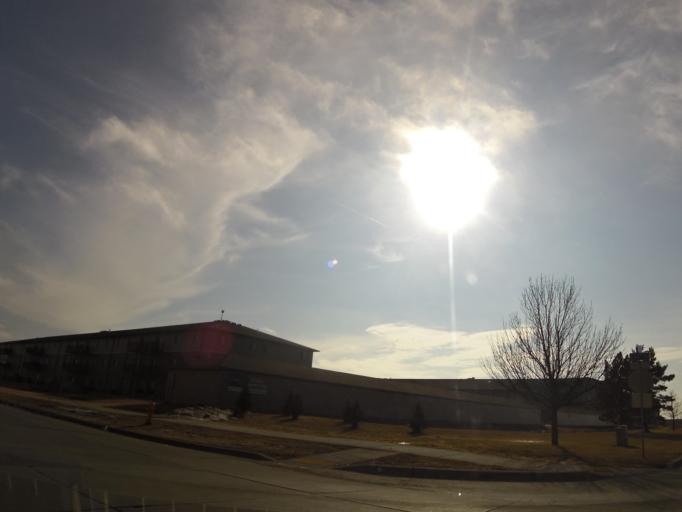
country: US
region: North Dakota
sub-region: Grand Forks County
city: Grand Forks
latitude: 47.8859
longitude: -97.0775
